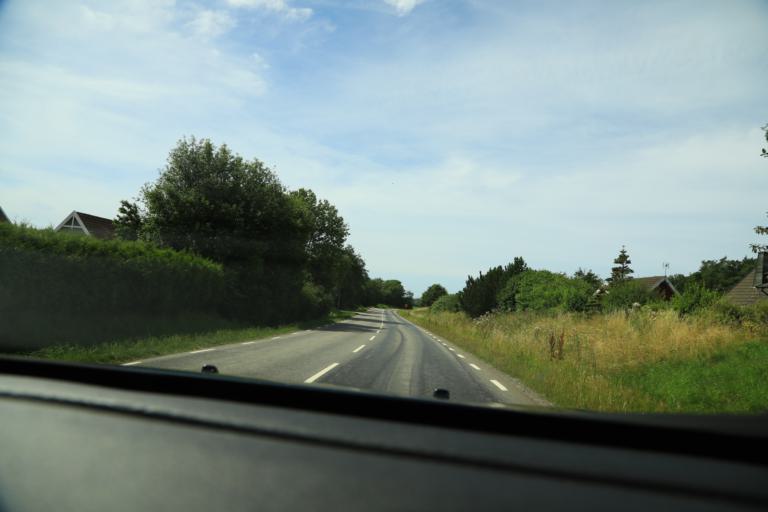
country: SE
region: Halland
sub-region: Varbergs Kommun
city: Varberg
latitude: 57.1414
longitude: 12.2860
